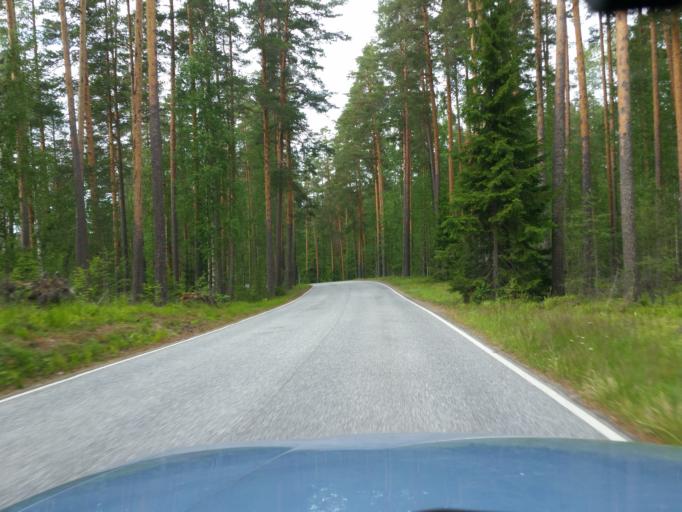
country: FI
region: Southern Savonia
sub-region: Savonlinna
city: Sulkava
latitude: 61.7880
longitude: 28.4253
